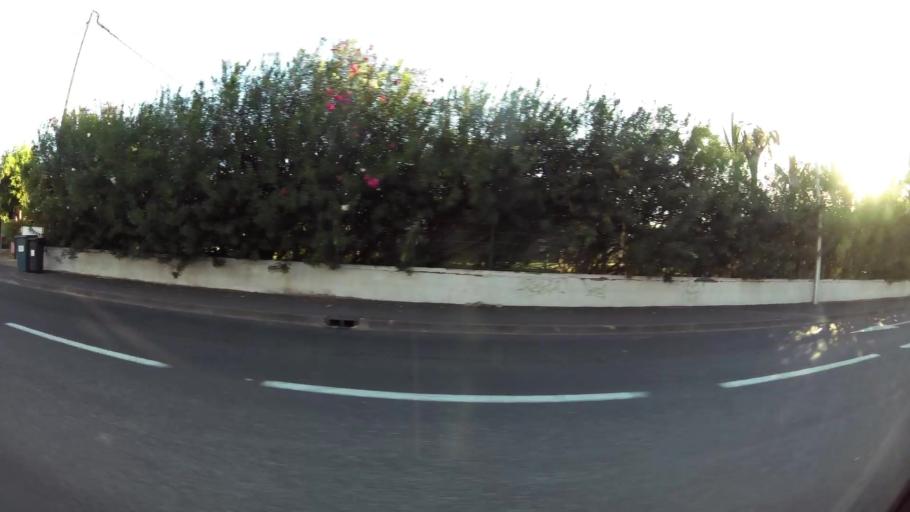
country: RE
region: Reunion
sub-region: Reunion
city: Trois-Bassins
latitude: -21.0928
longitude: 55.2361
